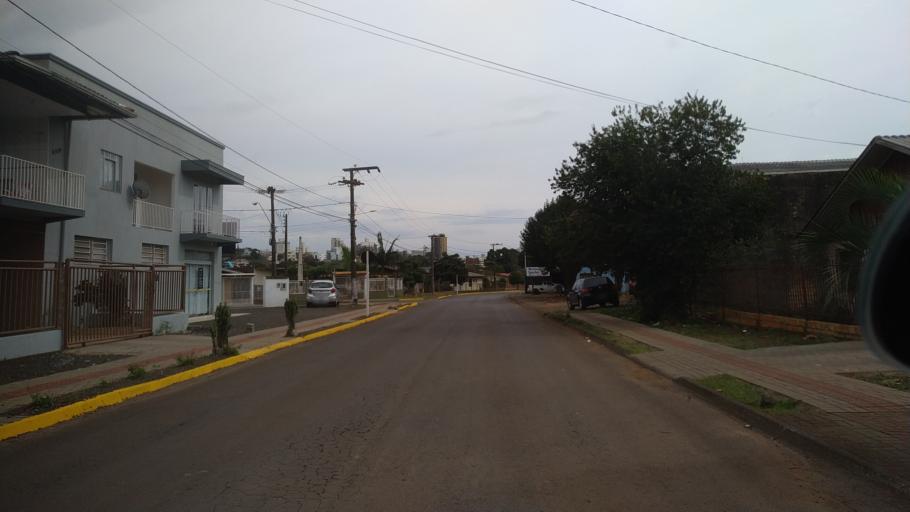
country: BR
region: Santa Catarina
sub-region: Chapeco
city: Chapeco
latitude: -27.1142
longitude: -52.6008
